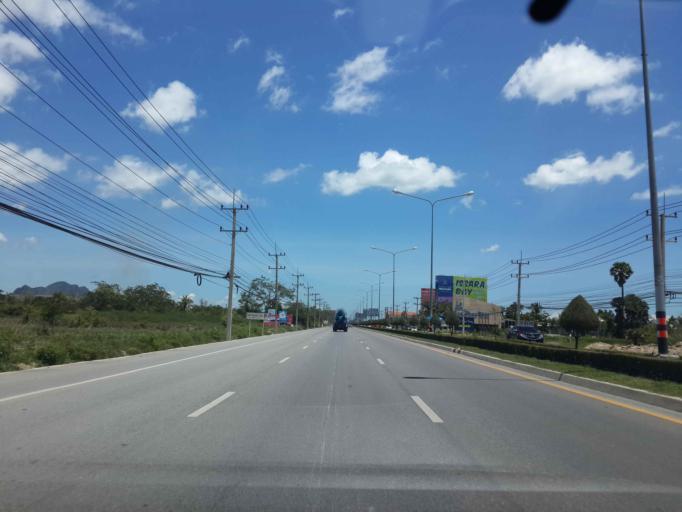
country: TH
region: Phetchaburi
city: Cha-am
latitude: 12.7571
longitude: 99.9626
